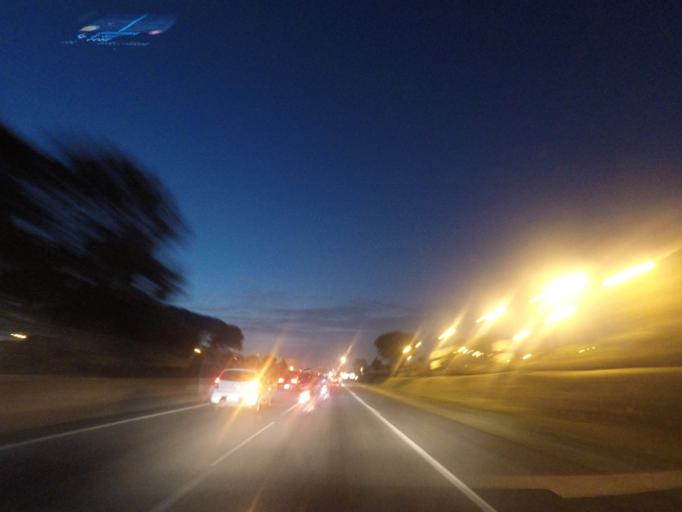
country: BR
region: Parana
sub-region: Pinhais
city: Pinhais
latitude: -25.4553
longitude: -49.2242
